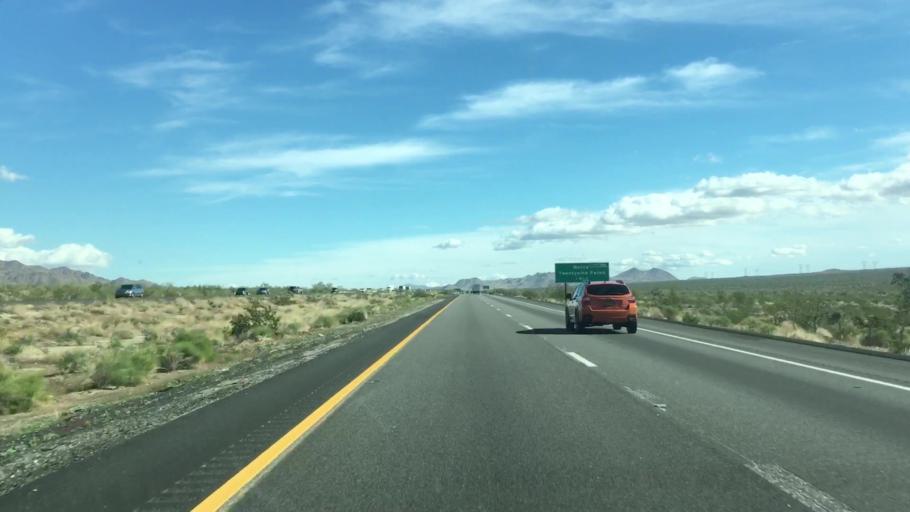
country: US
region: California
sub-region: Riverside County
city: Mecca
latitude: 33.6612
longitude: -115.8267
